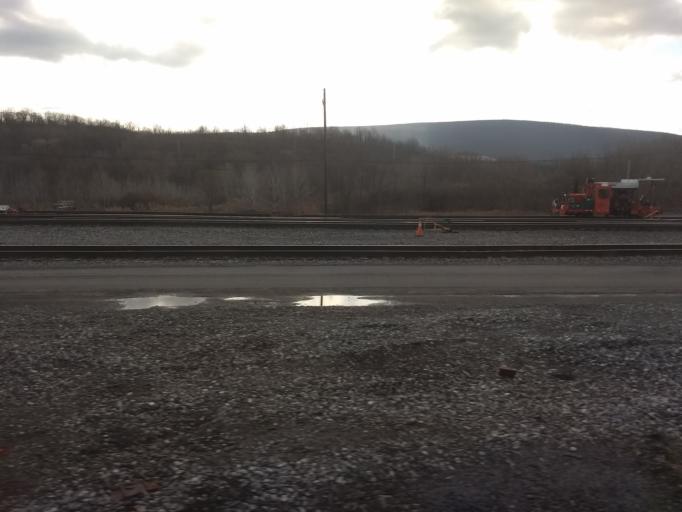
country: US
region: Pennsylvania
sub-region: Blair County
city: Greenwood
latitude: 40.5393
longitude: -78.3772
